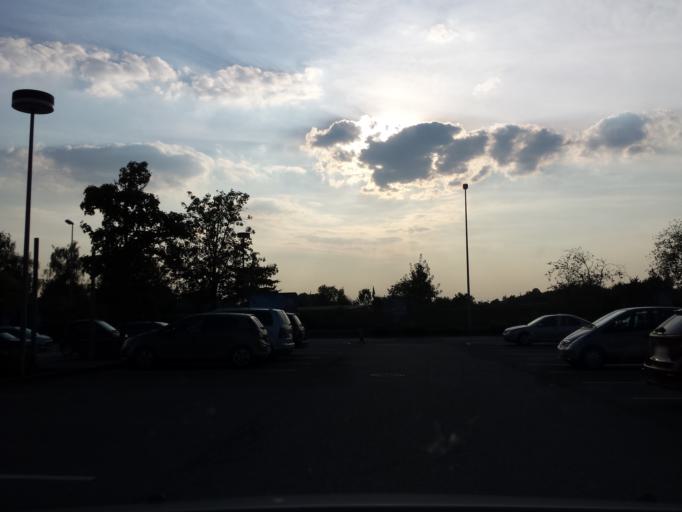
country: DE
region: Bavaria
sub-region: Swabia
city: Friedberg
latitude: 48.3545
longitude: 10.9697
